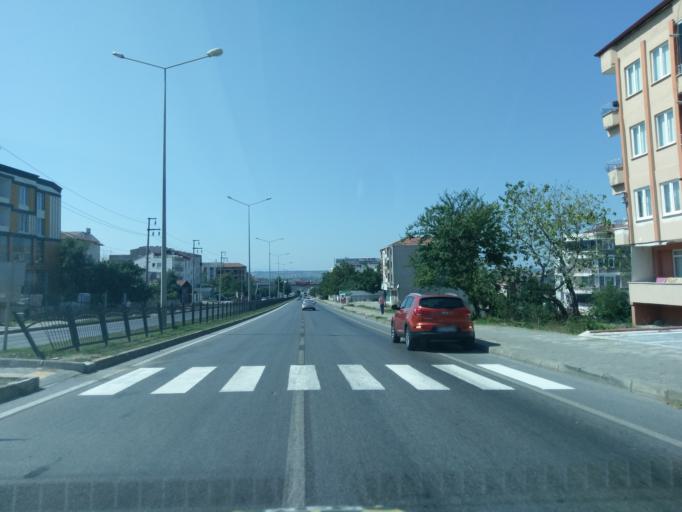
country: TR
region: Samsun
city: Bafra
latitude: 41.5561
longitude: 35.9133
